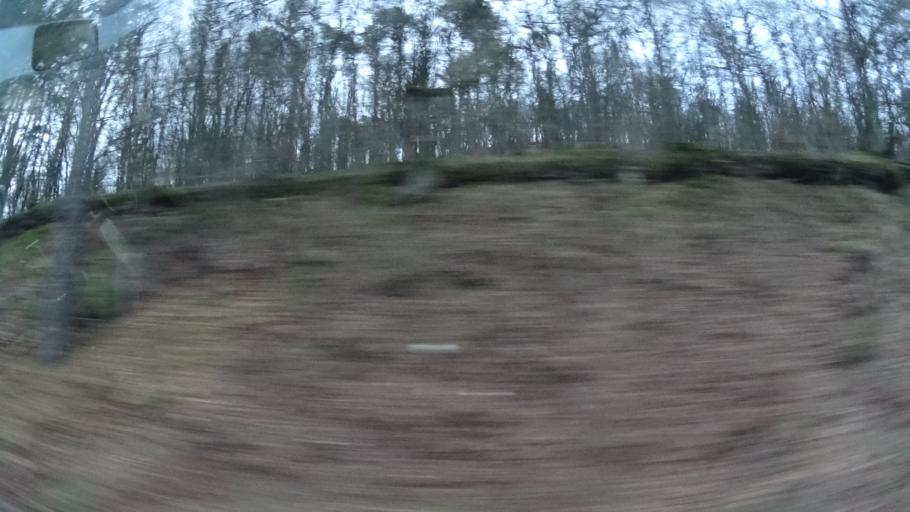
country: DE
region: Rheinland-Pfalz
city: Ellweiler
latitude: 49.6128
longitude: 7.1502
